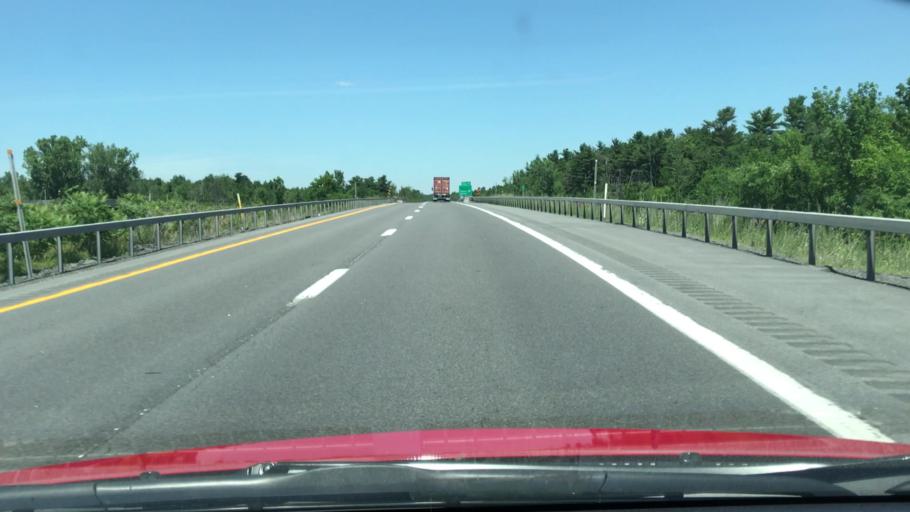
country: US
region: New York
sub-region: Clinton County
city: Champlain
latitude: 44.8832
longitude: -73.4512
